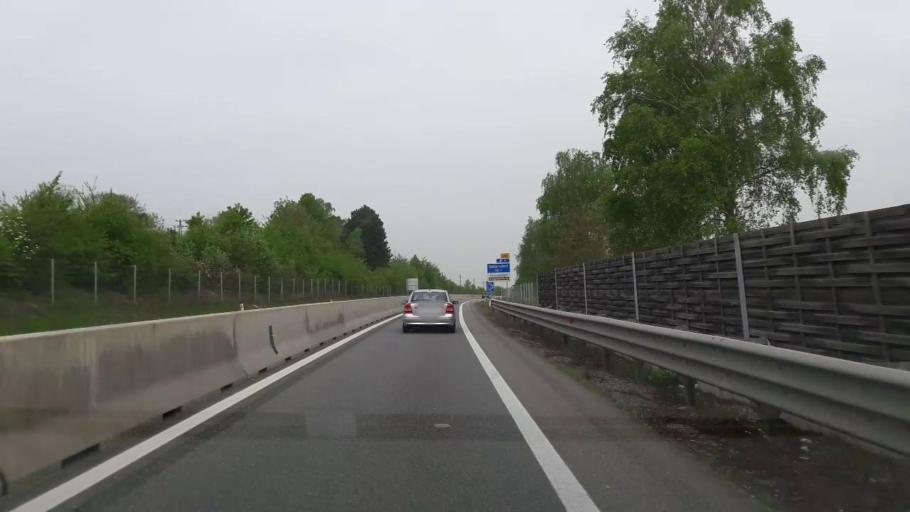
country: AT
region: Lower Austria
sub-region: Politischer Bezirk Hollabrunn
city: Gollersdorf
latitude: 48.4878
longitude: 16.1153
